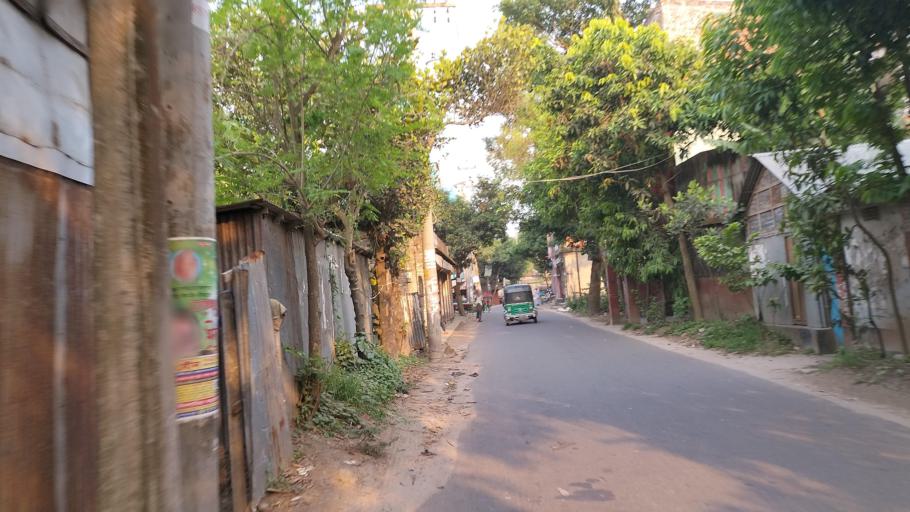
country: BD
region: Dhaka
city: Azimpur
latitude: 23.6648
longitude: 90.3301
